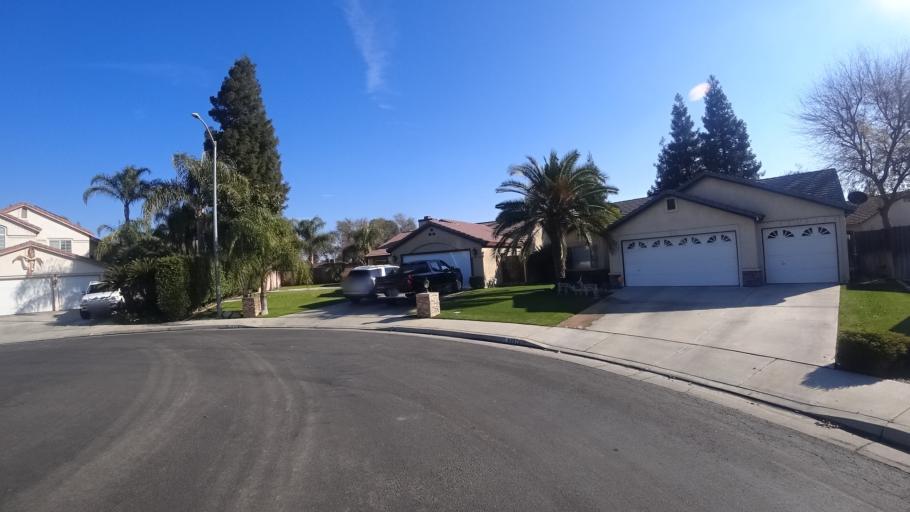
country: US
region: California
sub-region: Kern County
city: Greenacres
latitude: 35.3228
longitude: -119.1103
